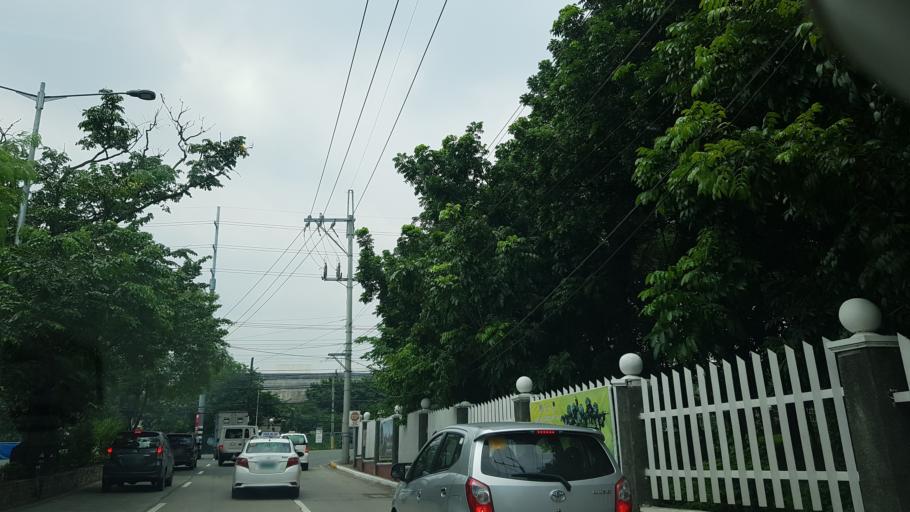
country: PH
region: Metro Manila
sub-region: Makati City
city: Makati City
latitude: 14.5341
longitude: 121.0409
